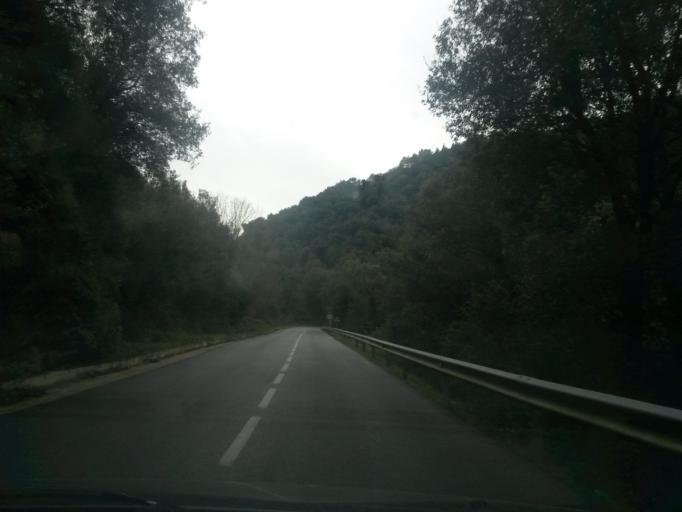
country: ES
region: Catalonia
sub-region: Provincia de Girona
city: la Cellera de Ter
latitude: 41.9521
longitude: 2.5939
